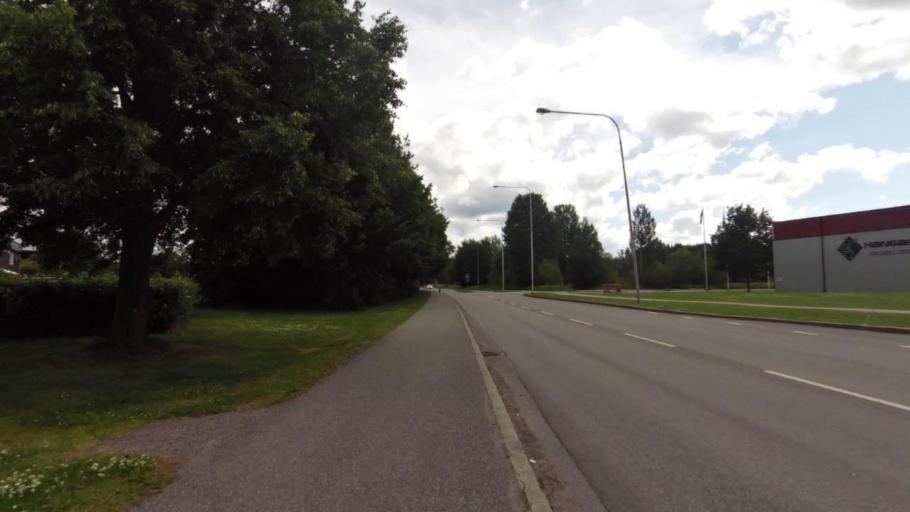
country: SE
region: OEstergoetland
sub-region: Linkopings Kommun
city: Malmslatt
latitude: 58.4099
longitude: 15.5560
